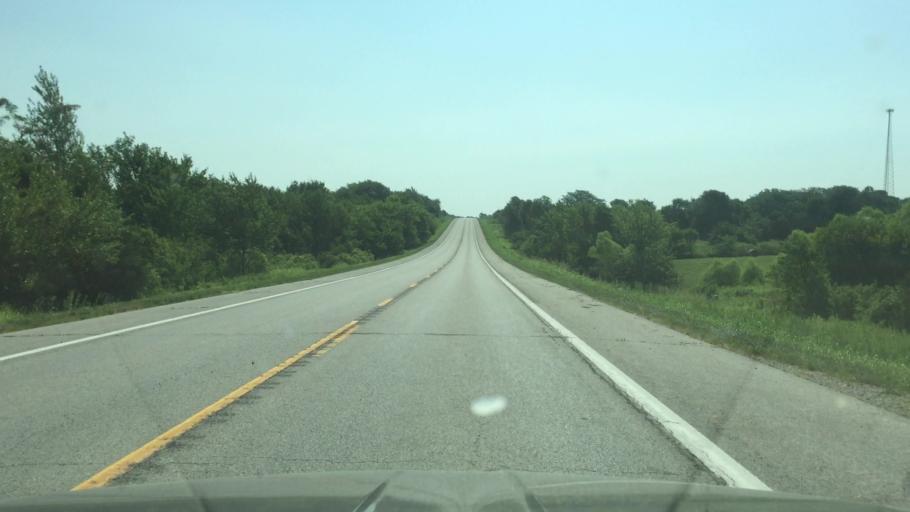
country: US
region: Missouri
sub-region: Pettis County
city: Sedalia
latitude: 38.6940
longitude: -93.1058
